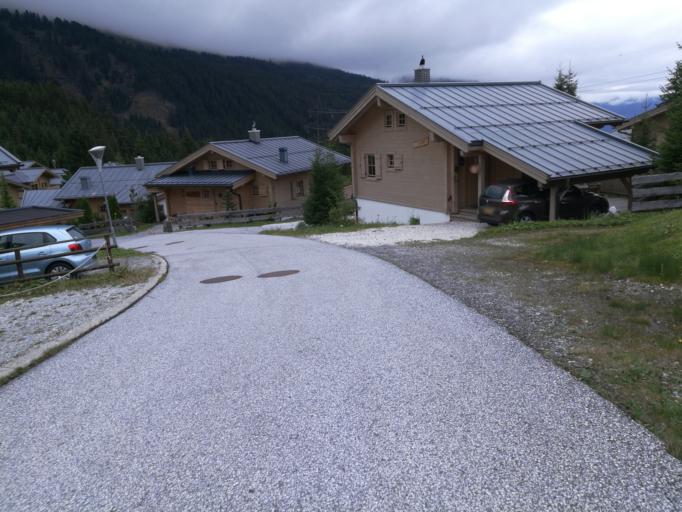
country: AT
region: Salzburg
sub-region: Politischer Bezirk Zell am See
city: Krimml
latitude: 47.2487
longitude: 12.1250
